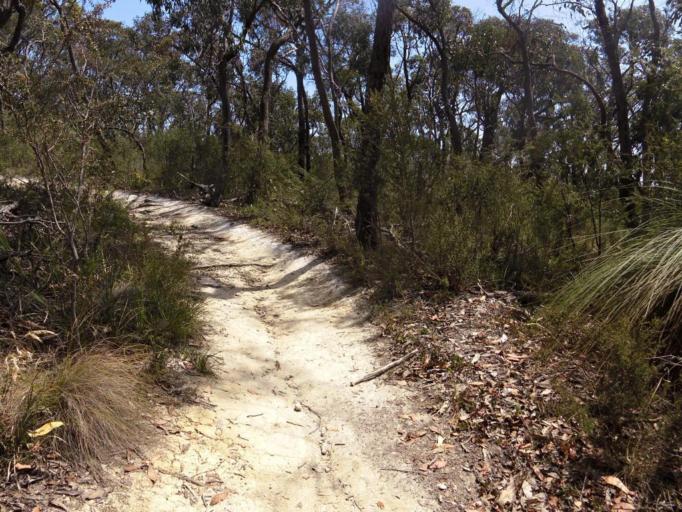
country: AU
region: Victoria
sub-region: Melton
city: Melton West
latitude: -37.5046
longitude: 144.5479
